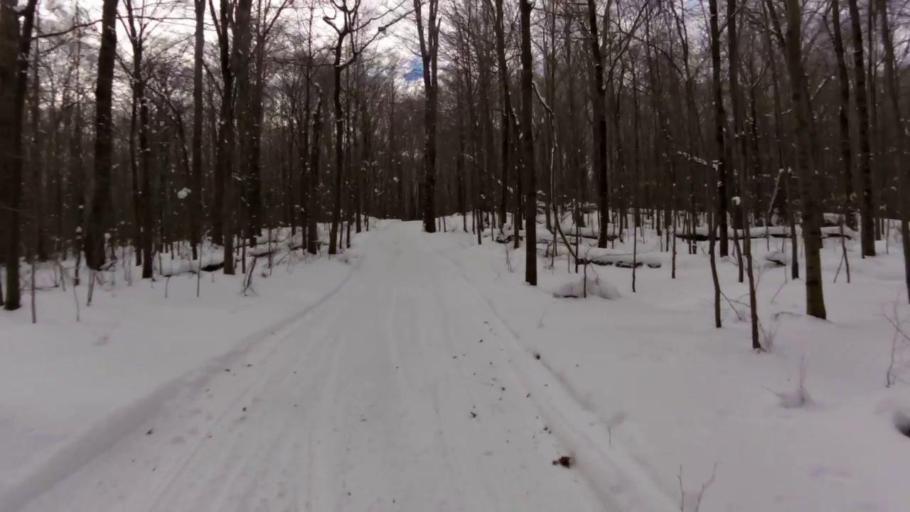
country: US
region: Pennsylvania
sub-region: McKean County
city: Bradford
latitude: 42.0264
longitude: -78.7381
